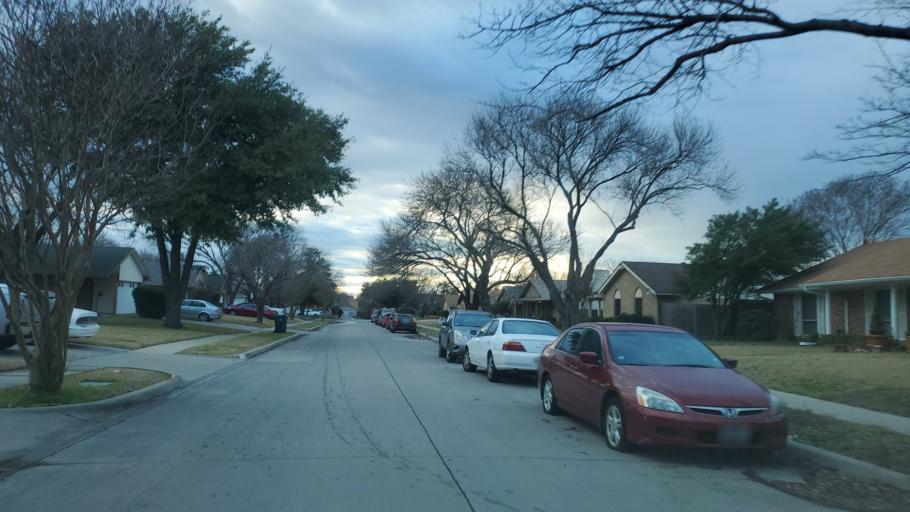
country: US
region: Texas
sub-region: Dallas County
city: Carrollton
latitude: 32.9919
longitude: -96.8855
